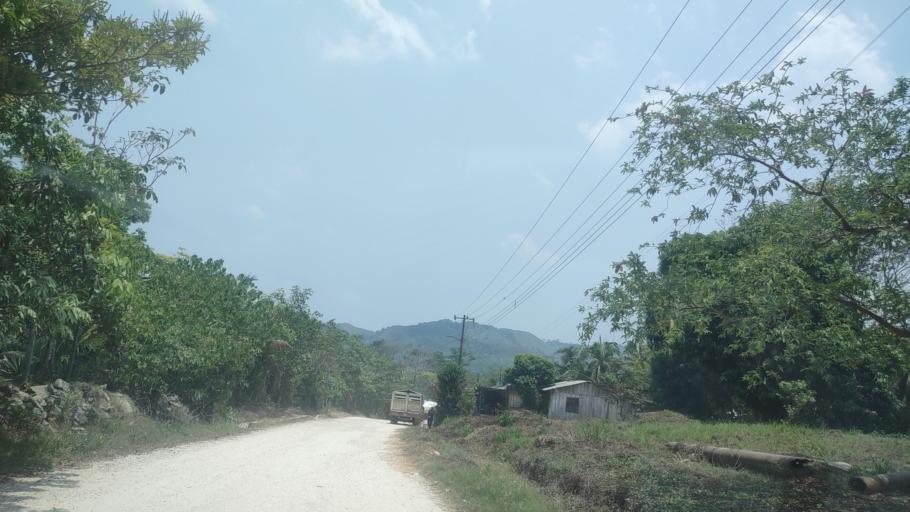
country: MX
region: Chiapas
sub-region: Tecpatan
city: Raudales Malpaso
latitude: 17.4593
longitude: -93.8011
